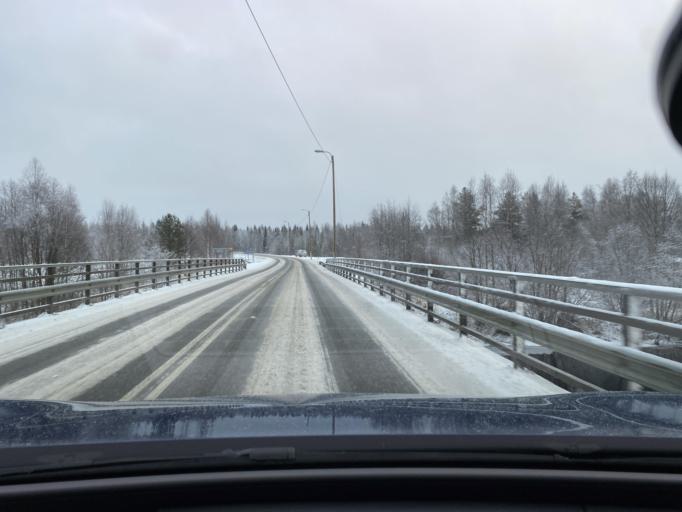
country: FI
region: Lapland
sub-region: Rovaniemi
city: Ranua
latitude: 65.9986
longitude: 26.2094
